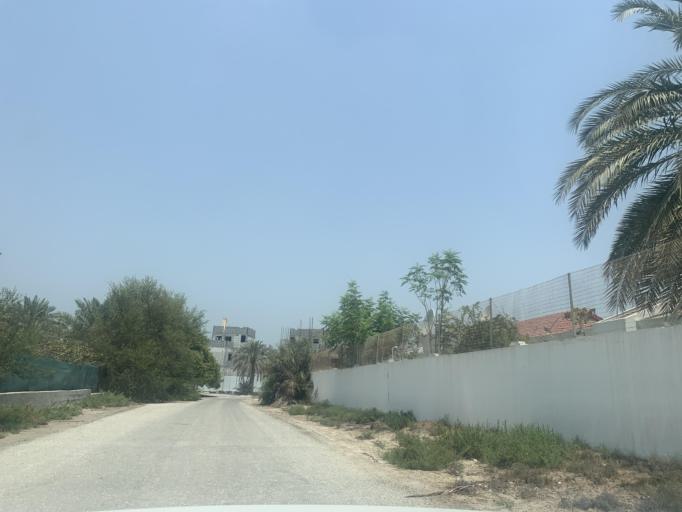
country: BH
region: Central Governorate
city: Madinat Hamad
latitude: 26.1487
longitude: 50.4625
